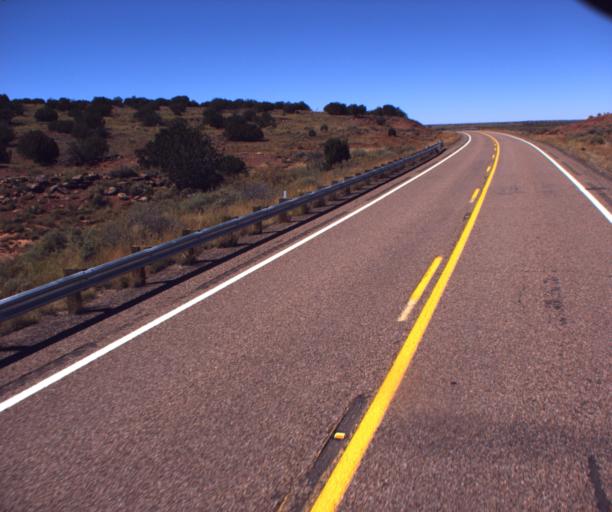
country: US
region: Arizona
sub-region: Apache County
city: Saint Johns
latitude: 34.5869
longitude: -109.5451
